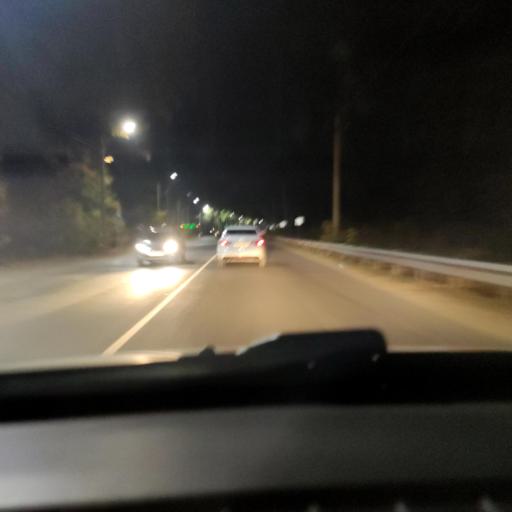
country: RU
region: Voronezj
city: Podgornoye
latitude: 51.7850
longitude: 39.1848
